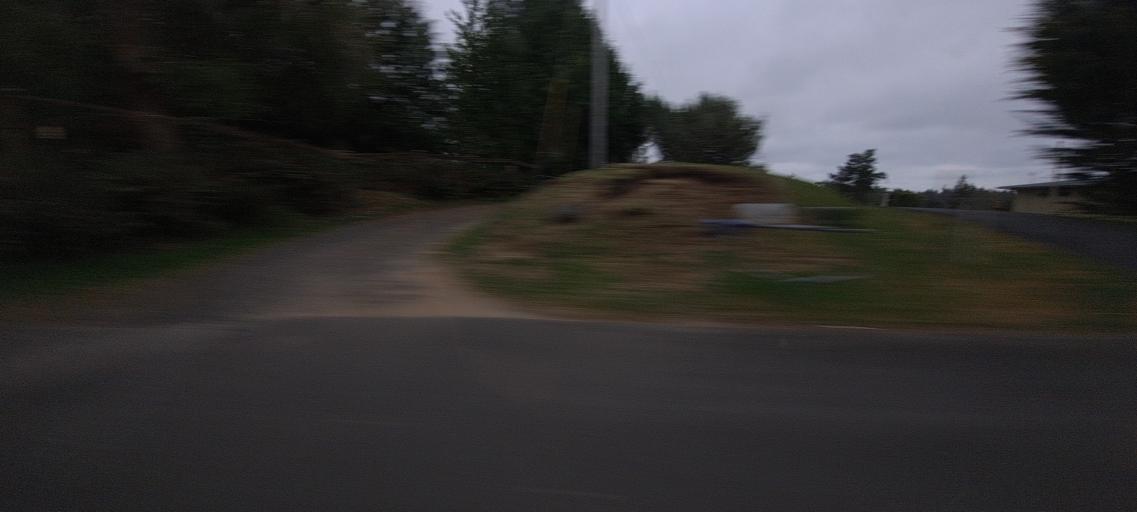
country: US
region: Oregon
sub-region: Clatsop County
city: Warrenton
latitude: 46.1364
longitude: -123.9304
